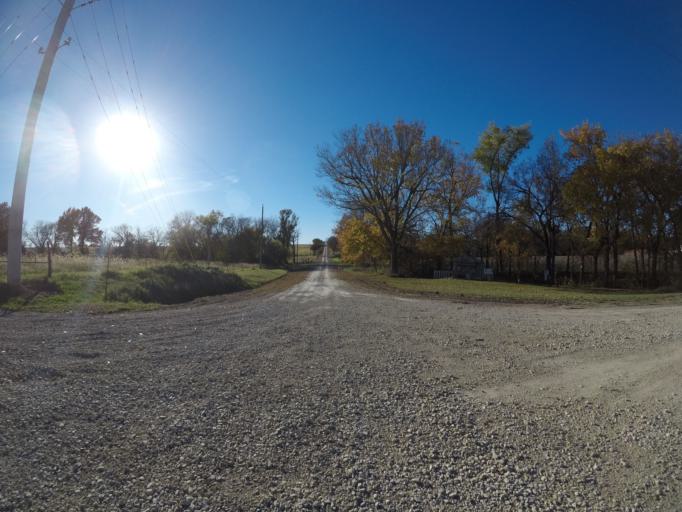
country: US
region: Kansas
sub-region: Riley County
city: Ogden
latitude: 39.2617
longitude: -96.7378
